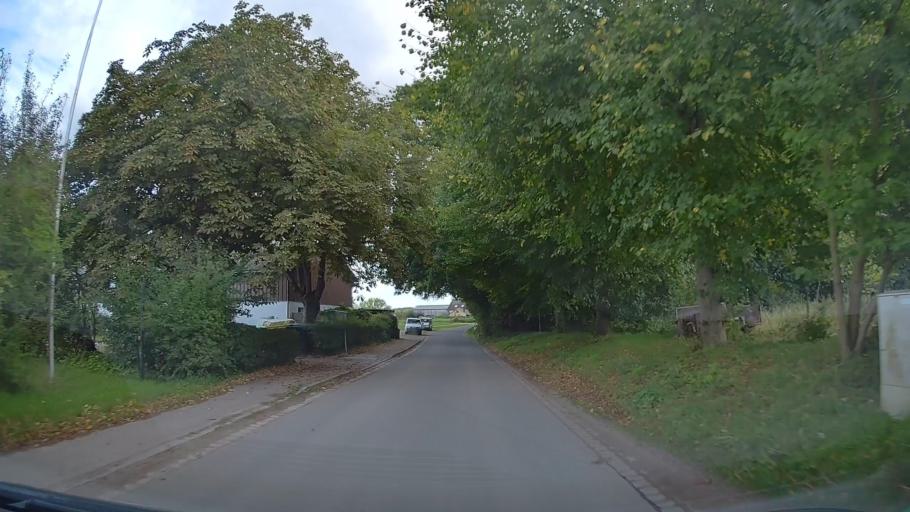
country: DE
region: Schleswig-Holstein
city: Steinberg
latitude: 54.7745
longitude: 9.8018
